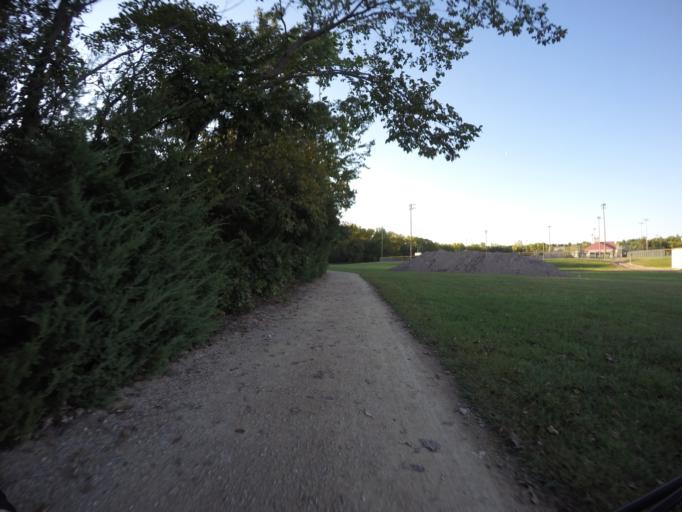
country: US
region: Kansas
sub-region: Riley County
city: Manhattan
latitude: 39.1856
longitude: -96.6339
